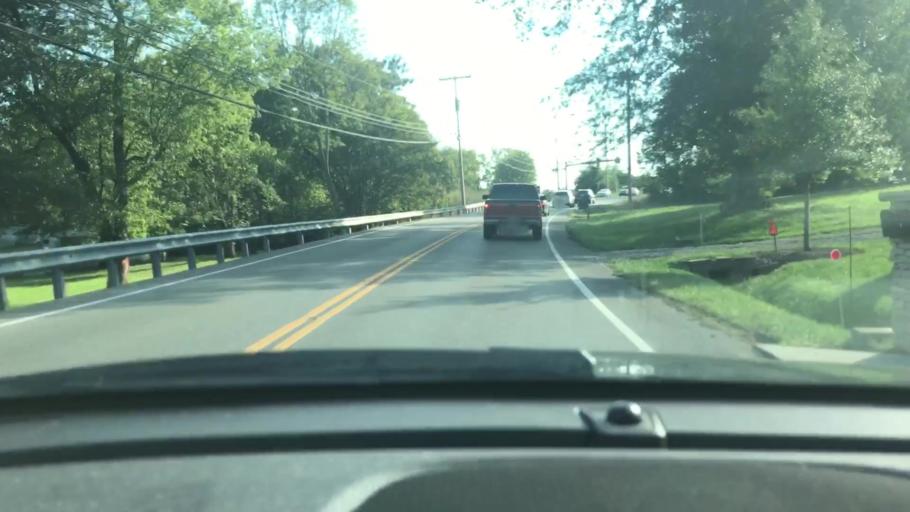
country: US
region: Tennessee
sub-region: Sumner County
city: Shackle Island
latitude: 36.3401
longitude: -86.6140
